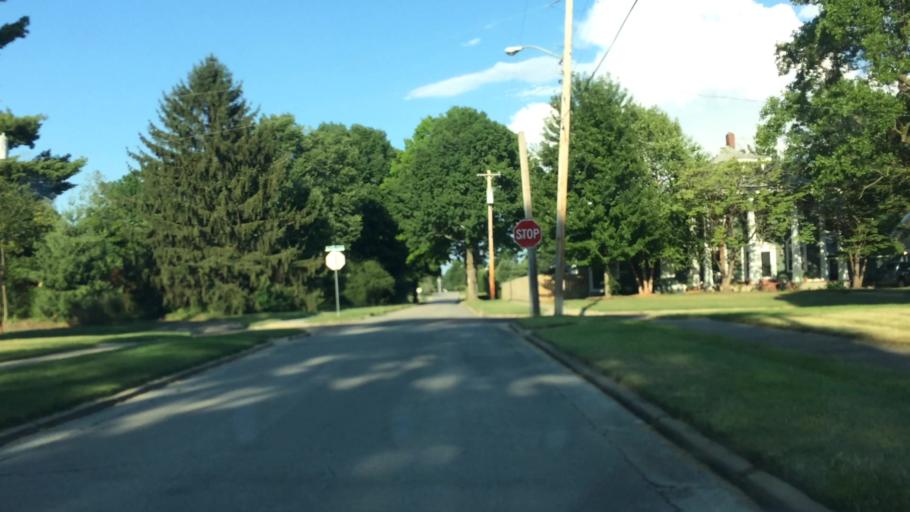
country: US
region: Missouri
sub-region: Greene County
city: Springfield
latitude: 37.1946
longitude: -93.2687
